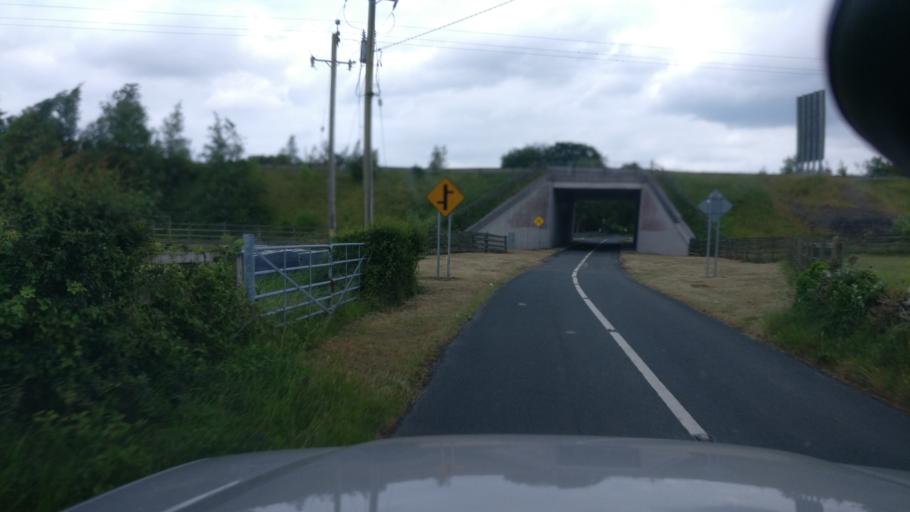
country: IE
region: Connaught
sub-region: County Galway
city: Ballinasloe
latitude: 53.3126
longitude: -8.2590
